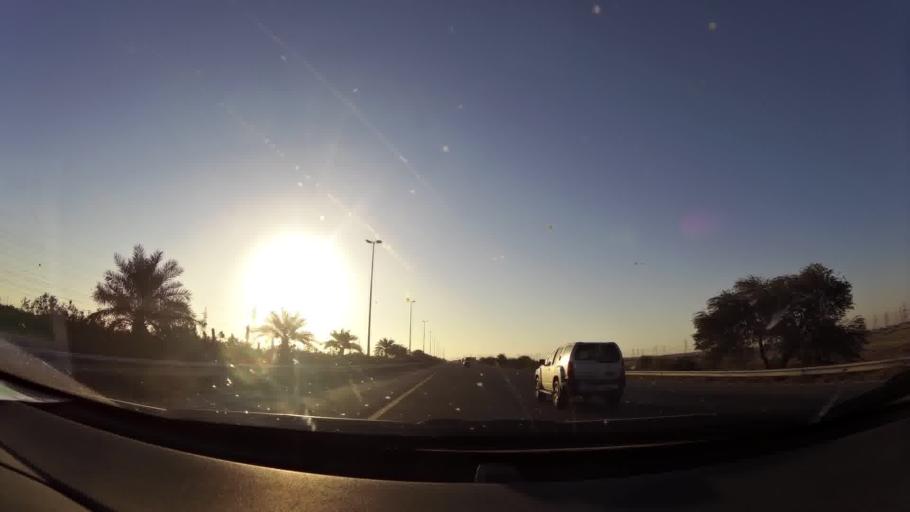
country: KW
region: Al Ahmadi
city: Al Fahahil
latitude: 28.9452
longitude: 48.1803
